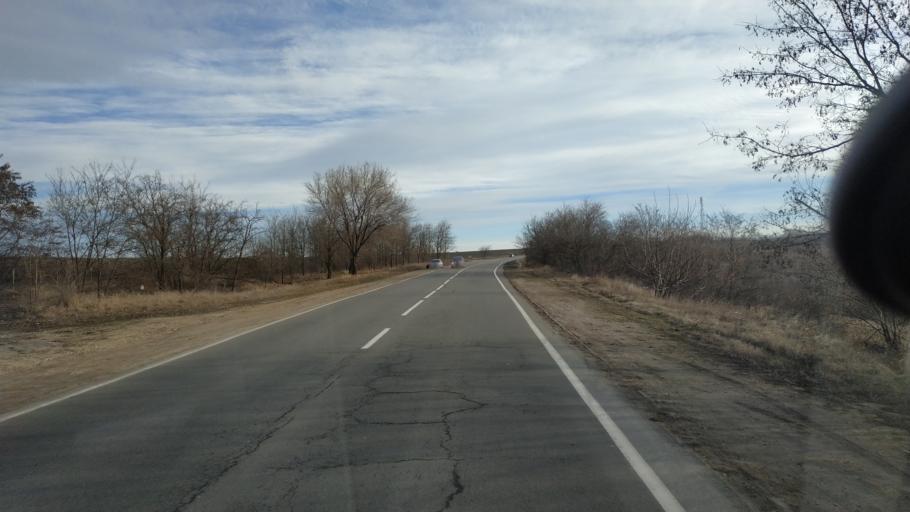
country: MD
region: Chisinau
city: Vadul lui Voda
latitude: 47.0854
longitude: 29.0402
